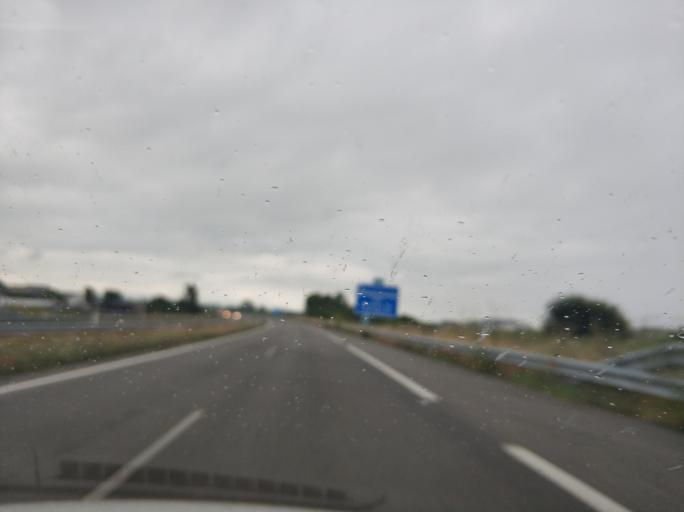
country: ES
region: Asturias
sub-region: Province of Asturias
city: Figueras
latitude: 43.5437
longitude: -7.0017
